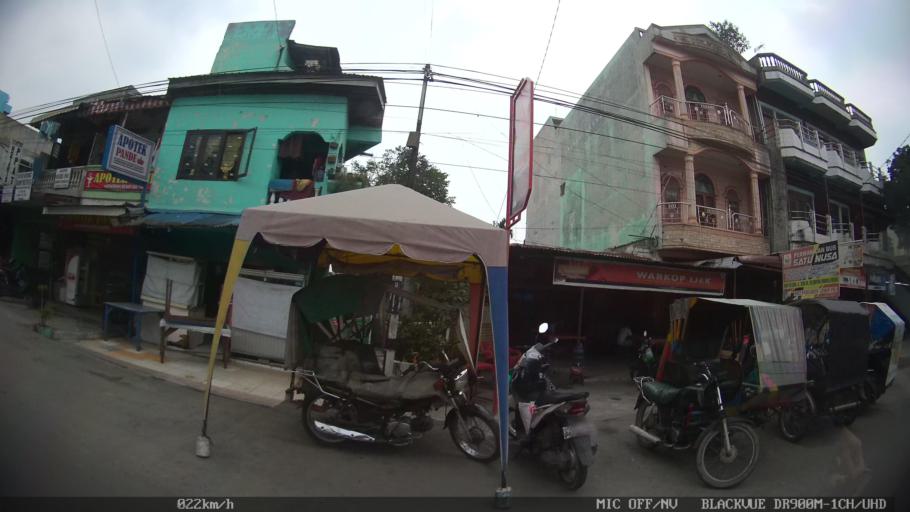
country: ID
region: North Sumatra
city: Medan
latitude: 3.5821
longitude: 98.7094
